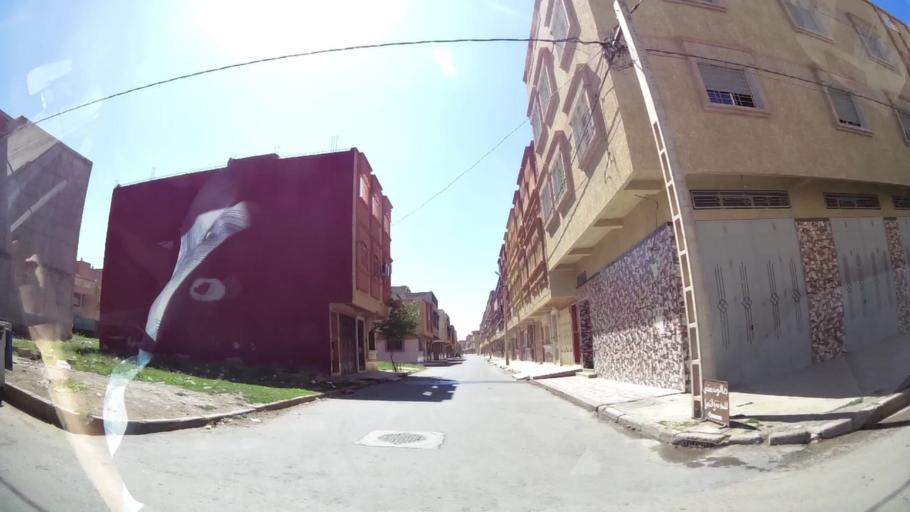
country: MA
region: Oriental
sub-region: Oujda-Angad
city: Oujda
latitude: 34.6837
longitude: -1.9385
